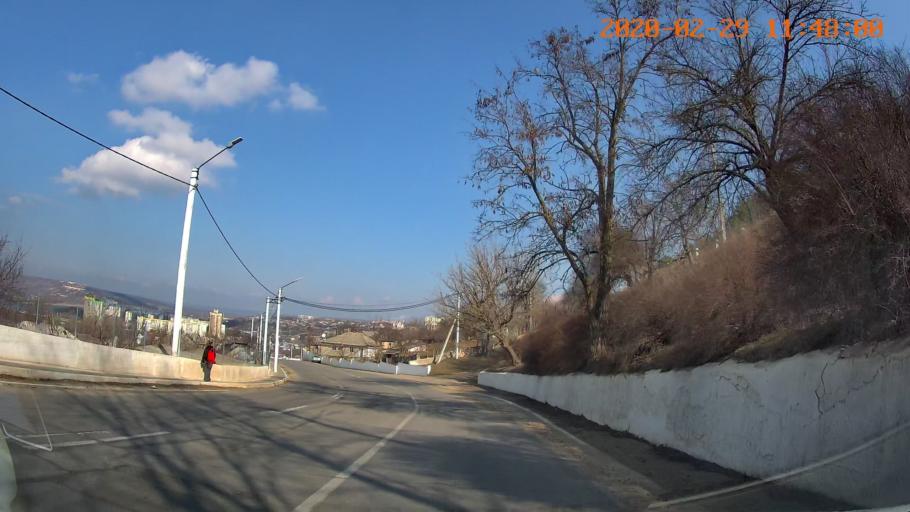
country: MD
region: Rezina
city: Rezina
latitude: 47.7452
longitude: 28.9887
